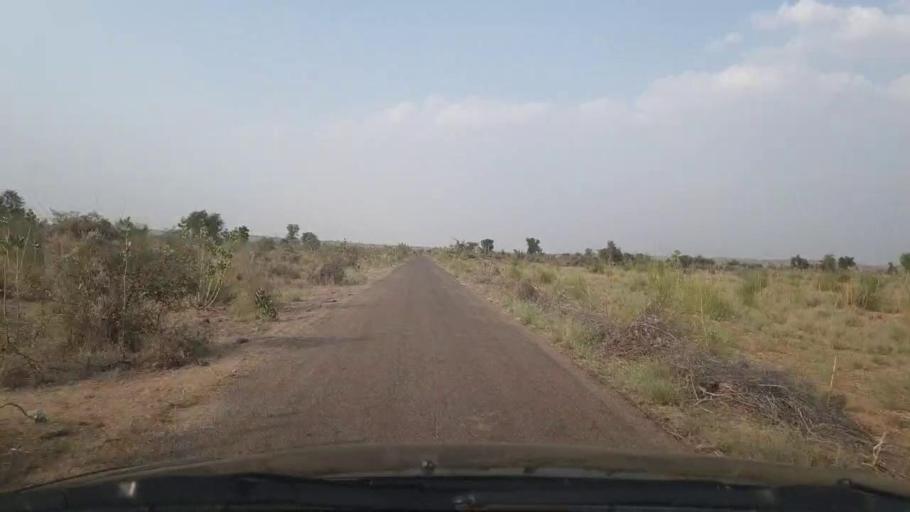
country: PK
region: Sindh
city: Islamkot
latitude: 25.0547
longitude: 70.5597
